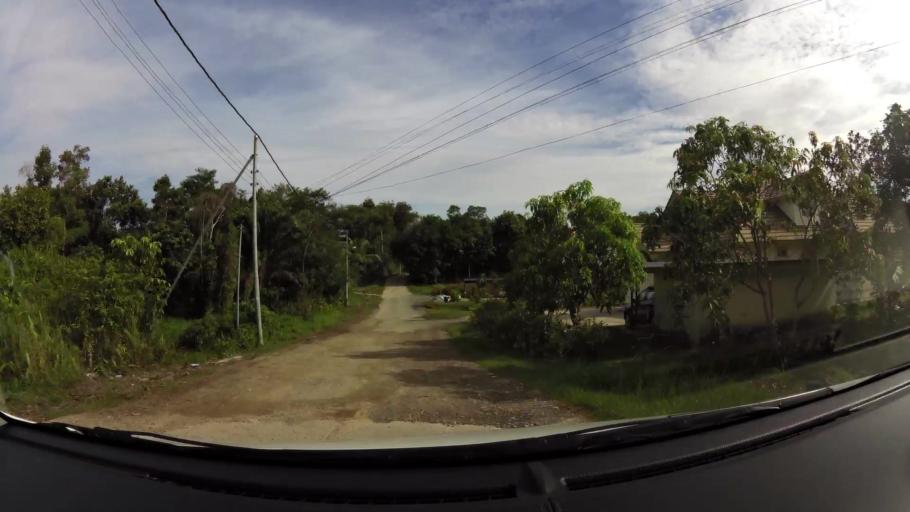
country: BN
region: Brunei and Muara
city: Bandar Seri Begawan
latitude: 4.9030
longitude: 114.8842
